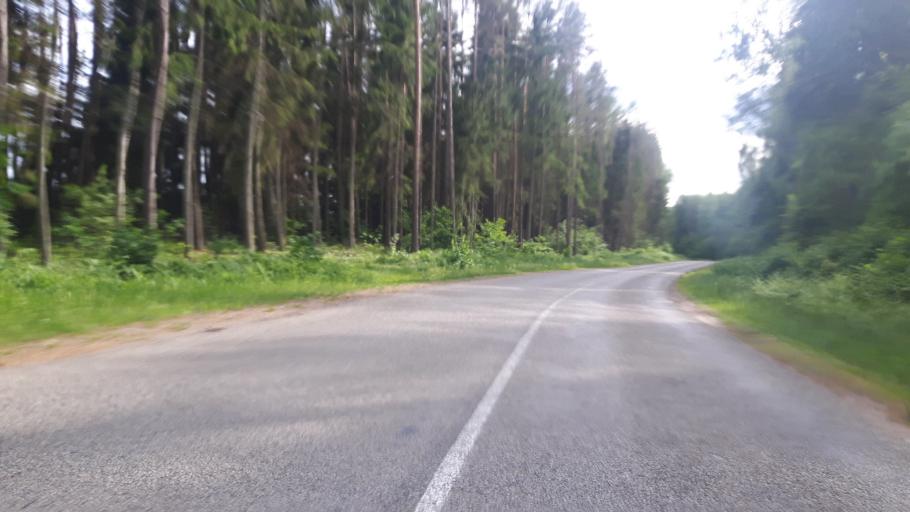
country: LV
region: Engure
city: Smarde
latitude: 56.9959
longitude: 23.3193
